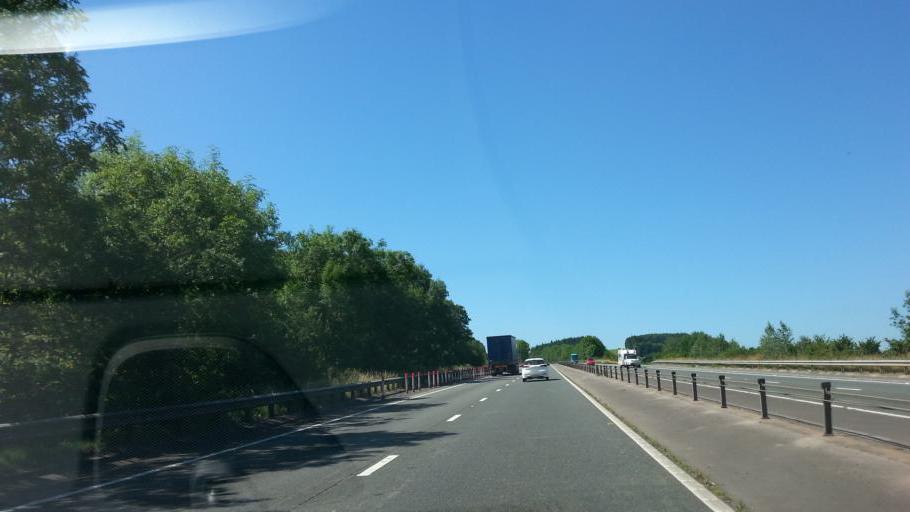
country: GB
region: Wales
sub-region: Newport
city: Langstone
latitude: 51.6265
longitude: -2.8998
